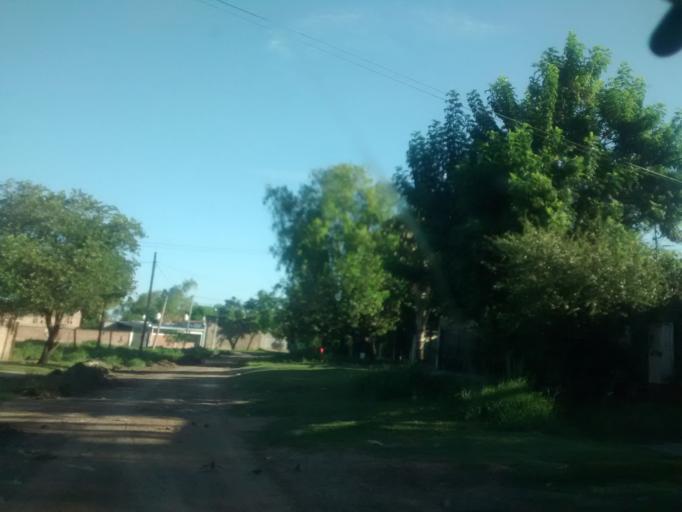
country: AR
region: Chaco
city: Resistencia
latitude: -27.4322
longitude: -58.9901
